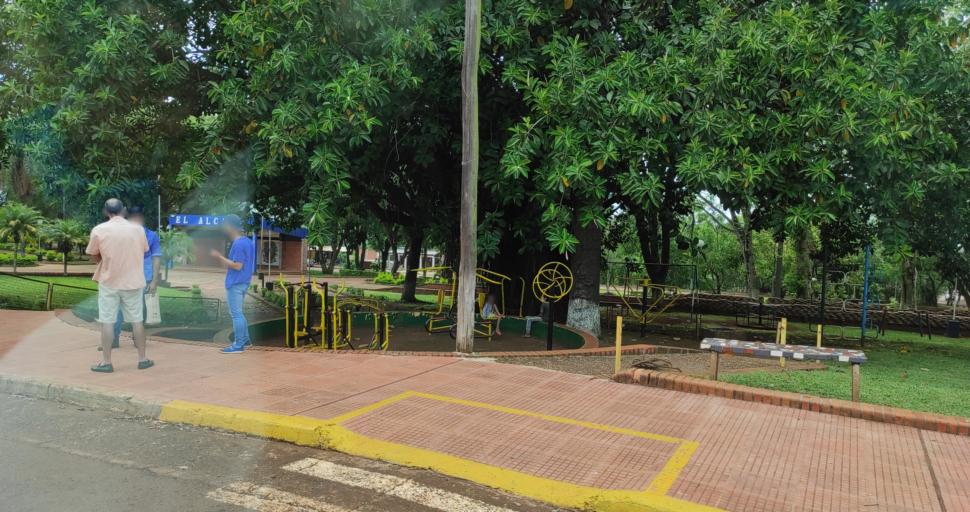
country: AR
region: Misiones
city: El Alcazar
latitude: -26.7171
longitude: -54.8136
